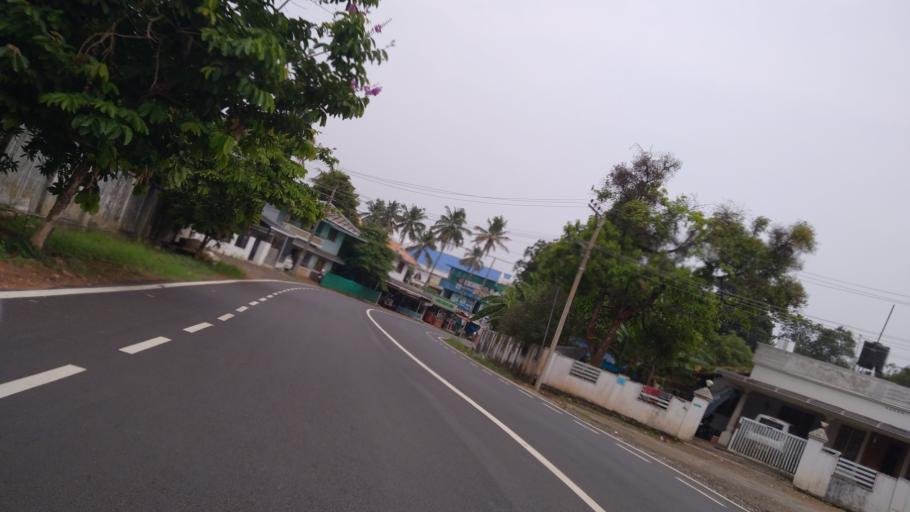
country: IN
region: Kerala
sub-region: Ernakulam
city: Angamali
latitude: 10.1802
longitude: 76.3974
